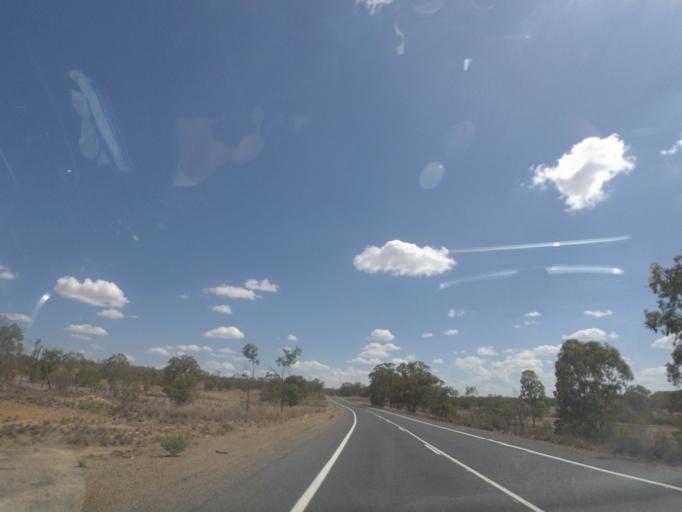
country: AU
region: Queensland
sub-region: Southern Downs
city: Warwick
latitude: -28.2227
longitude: 151.5535
